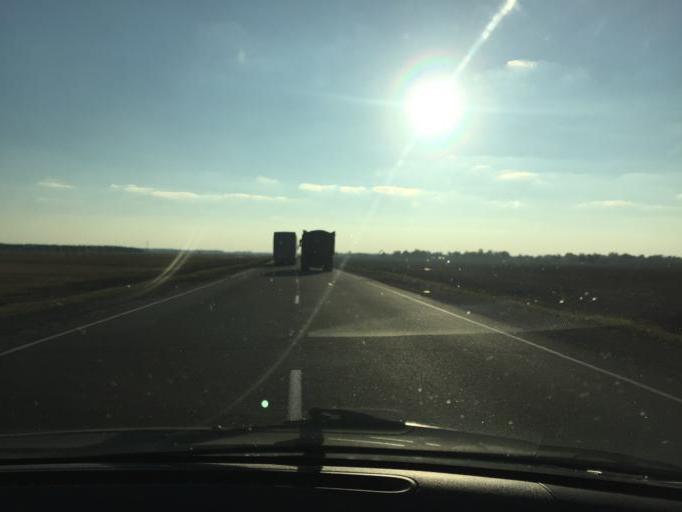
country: BY
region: Brest
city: Asnyezhytsy
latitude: 52.2922
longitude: 26.4200
